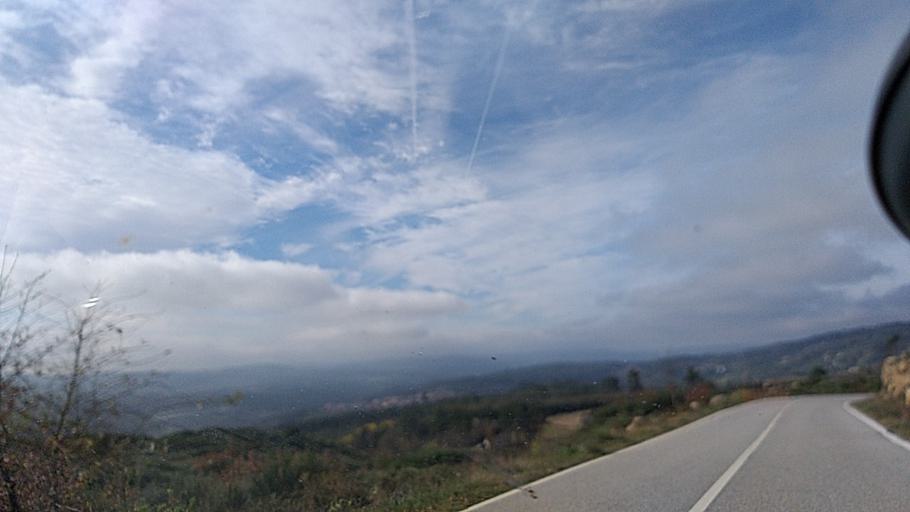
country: PT
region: Guarda
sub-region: Aguiar da Beira
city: Aguiar da Beira
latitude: 40.7515
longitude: -7.5459
